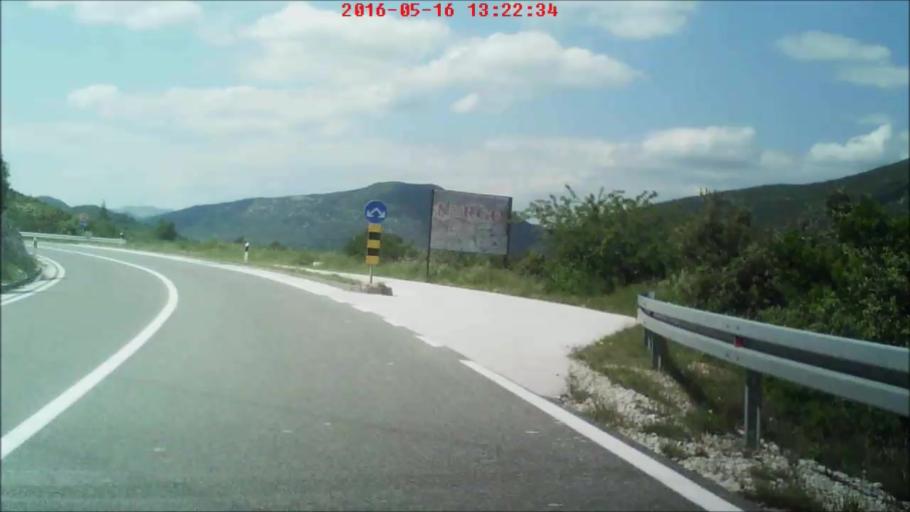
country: HR
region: Dubrovacko-Neretvanska
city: Ston
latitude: 42.8357
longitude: 17.7210
